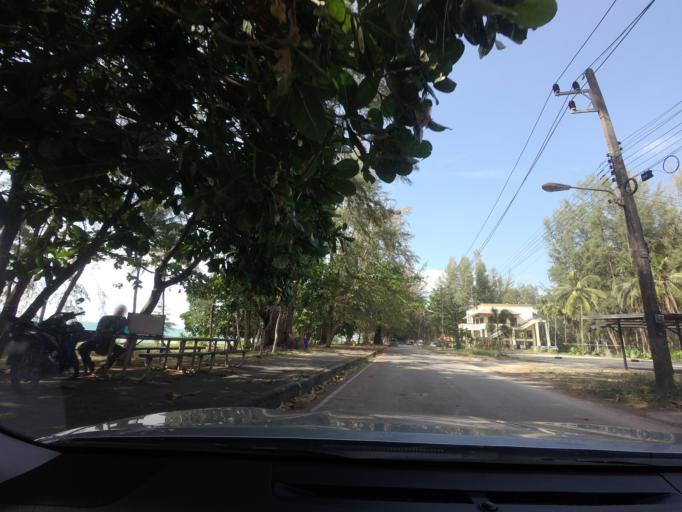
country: TH
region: Phangnga
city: Takua Pa
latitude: 8.7871
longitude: 98.2624
